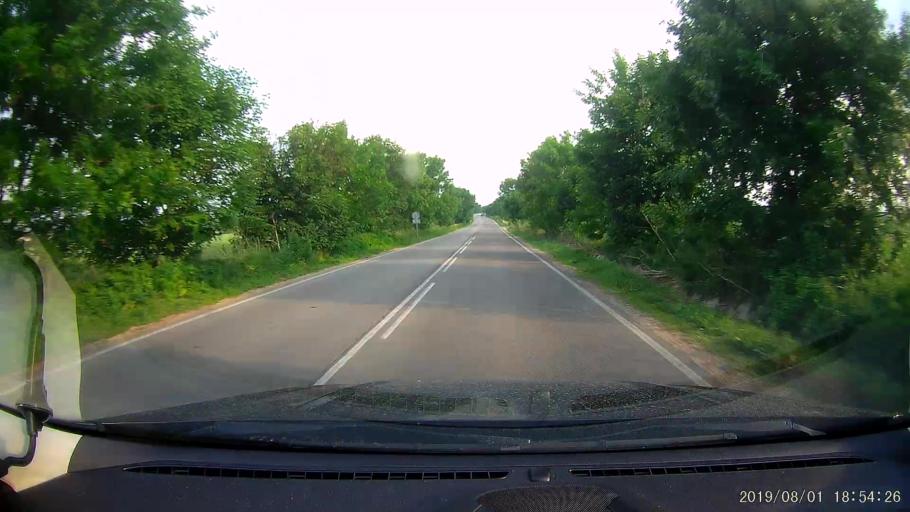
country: BG
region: Shumen
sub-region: Obshtina Shumen
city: Shumen
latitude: 43.1986
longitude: 27.0018
